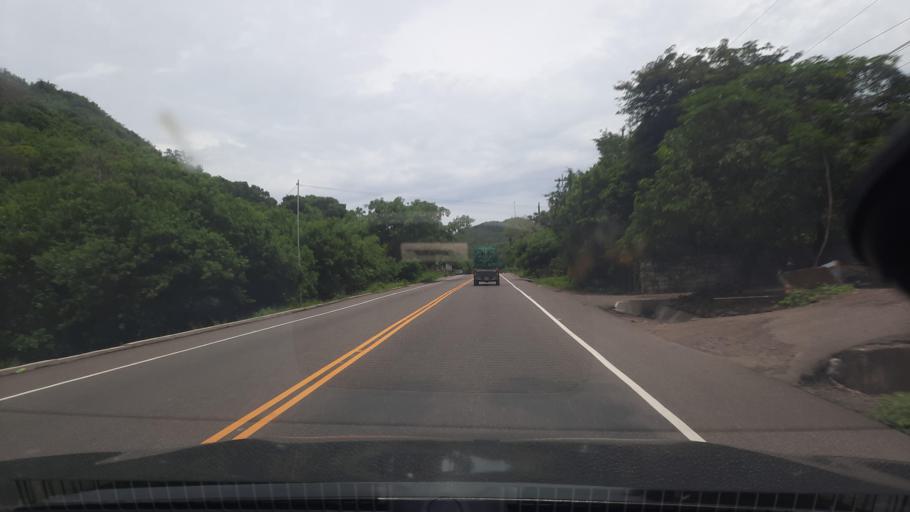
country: HN
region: Valle
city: Langue
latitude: 13.5687
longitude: -87.6718
